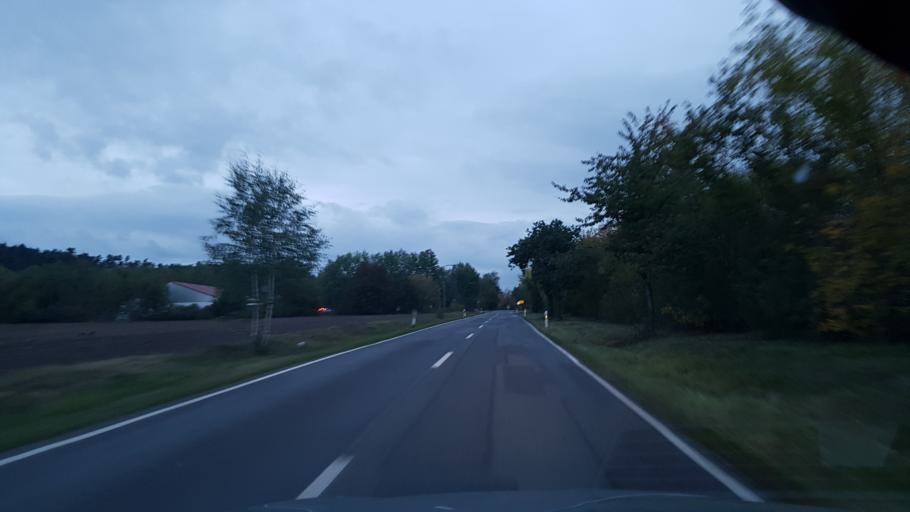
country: DE
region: Brandenburg
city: Groden
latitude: 51.4000
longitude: 13.5857
